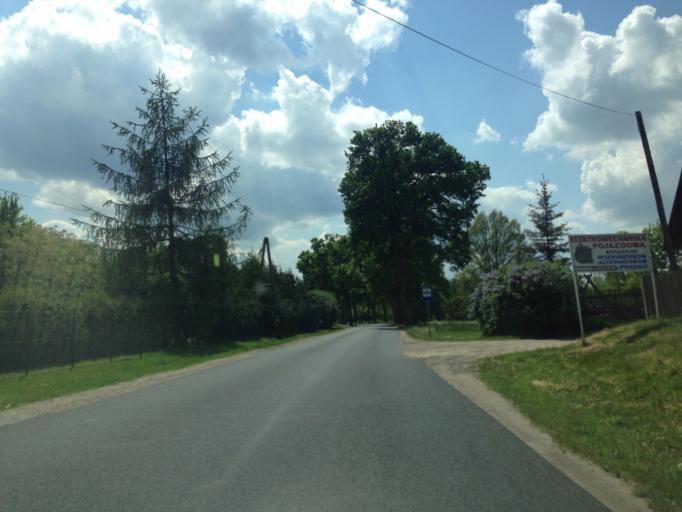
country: PL
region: Kujawsko-Pomorskie
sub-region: Powiat brodnicki
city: Brodnica
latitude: 53.2926
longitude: 19.3942
